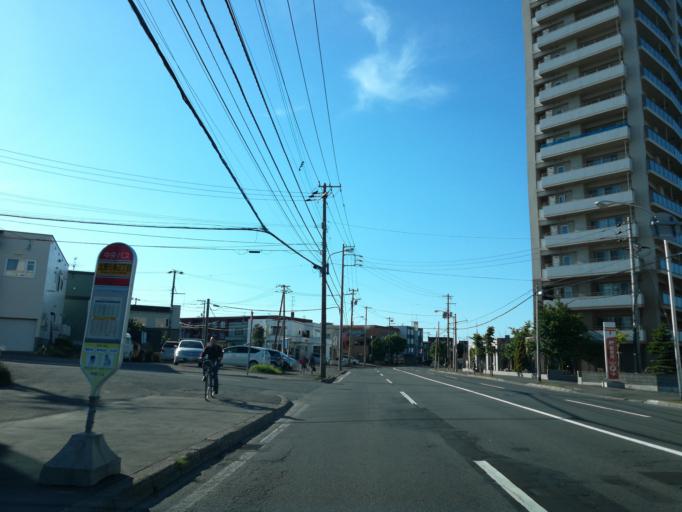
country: JP
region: Hokkaido
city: Sapporo
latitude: 43.0192
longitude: 141.4347
